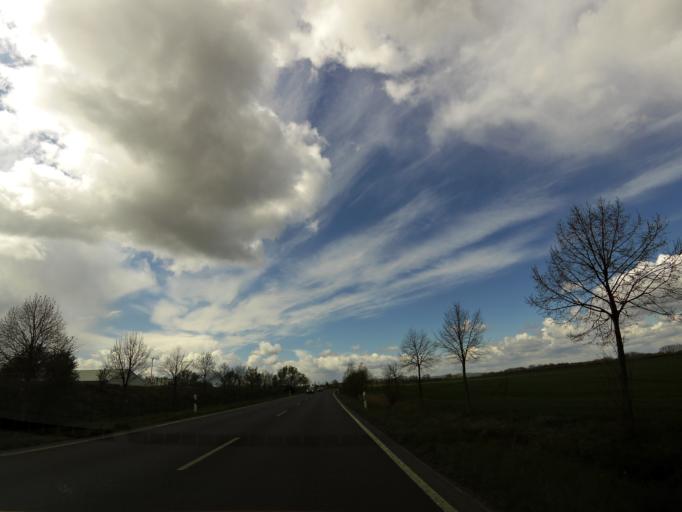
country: DE
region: Saxony-Anhalt
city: Groeningen
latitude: 51.9405
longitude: 11.2452
